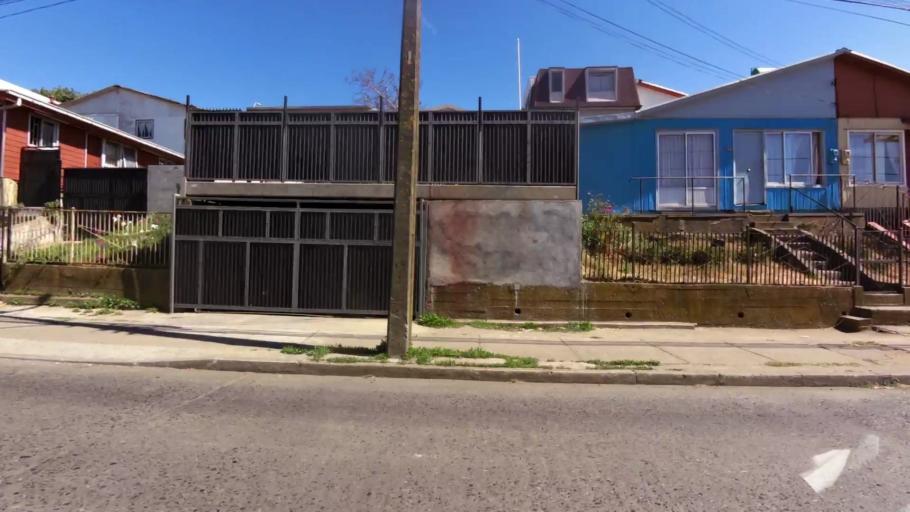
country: CL
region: Biobio
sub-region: Provincia de Concepcion
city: Penco
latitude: -36.7270
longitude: -72.9829
